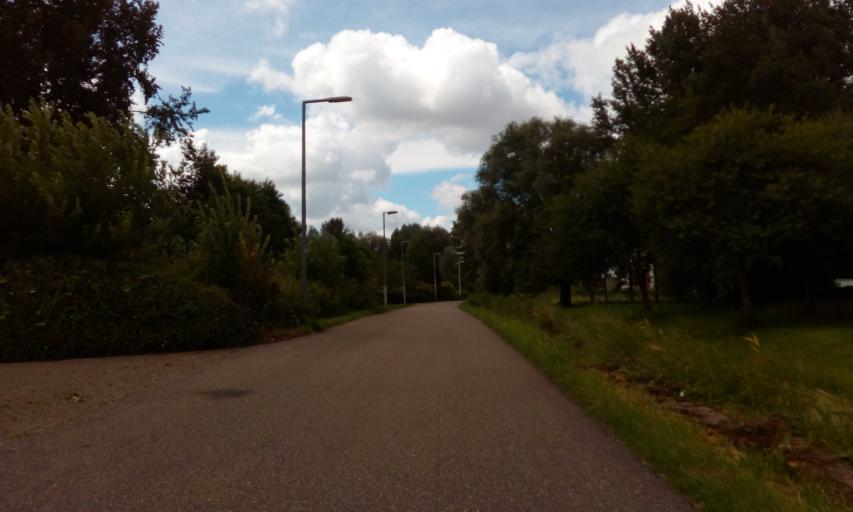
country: NL
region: South Holland
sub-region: Gemeente Barendrecht
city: Barendrecht
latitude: 51.8769
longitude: 4.5573
